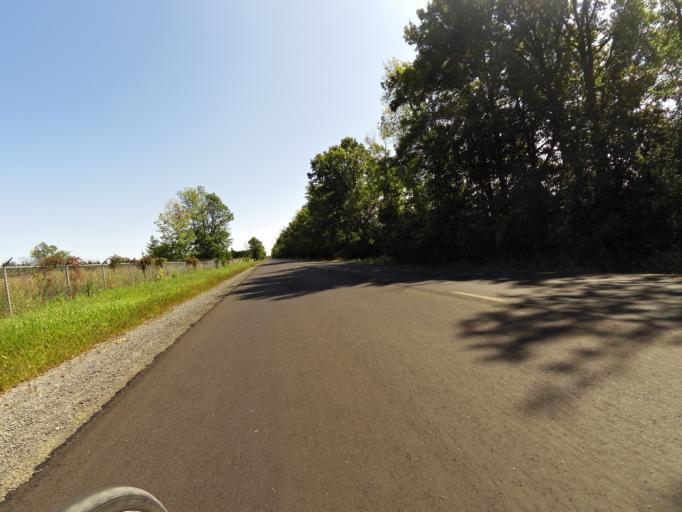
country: CA
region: Ontario
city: Bells Corners
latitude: 45.3677
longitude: -75.9250
